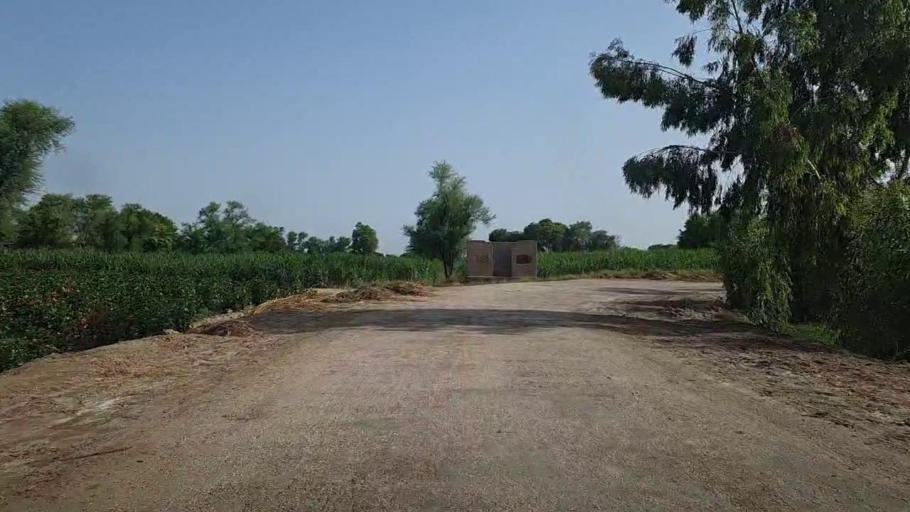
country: PK
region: Sindh
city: Pad Idan
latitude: 26.8536
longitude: 68.3308
